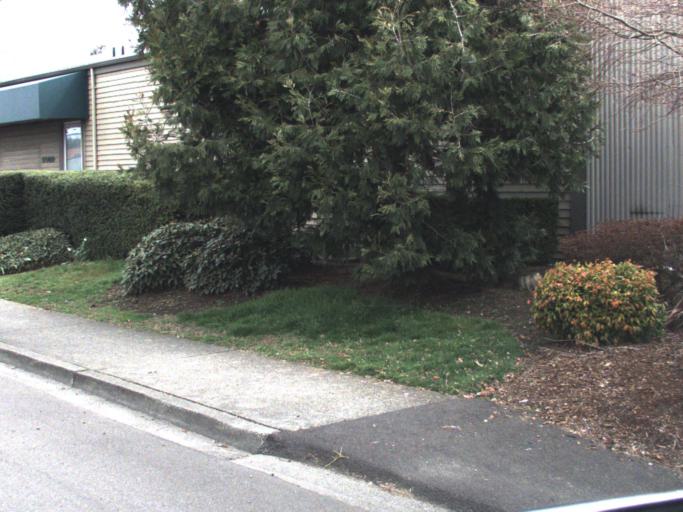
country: US
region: Washington
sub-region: King County
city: Normandy Park
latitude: 47.4433
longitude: -122.3342
